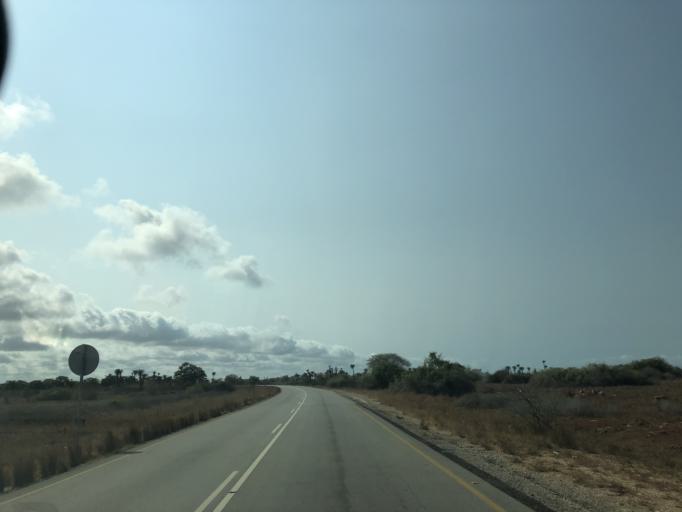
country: AO
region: Luanda
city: Luanda
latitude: -9.7058
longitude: 13.2166
